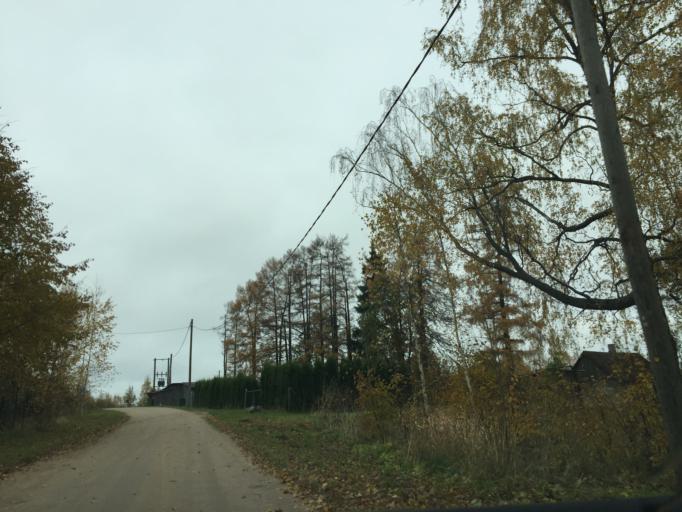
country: LV
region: Sigulda
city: Sigulda
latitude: 57.2421
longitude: 24.8296
